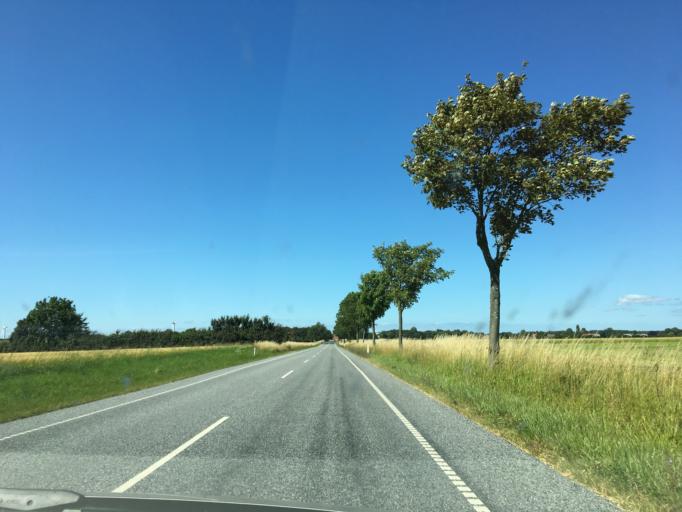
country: DK
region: South Denmark
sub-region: Langeland Kommune
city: Rudkobing
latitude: 54.7778
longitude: 10.7144
